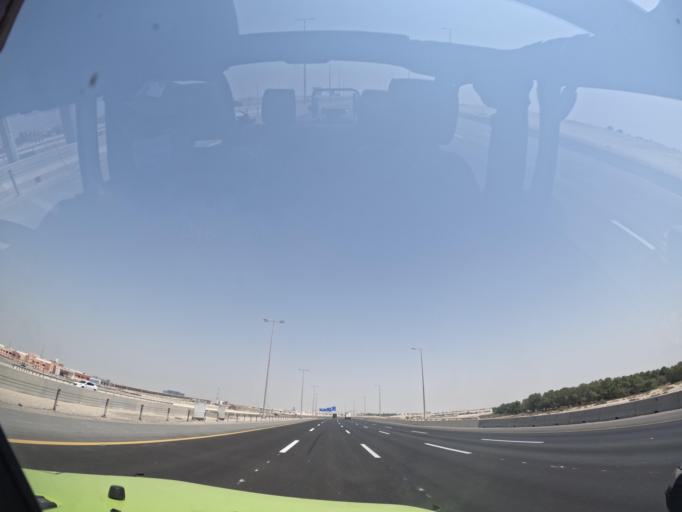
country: AE
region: Abu Dhabi
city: Abu Dhabi
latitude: 24.3006
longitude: 54.5908
